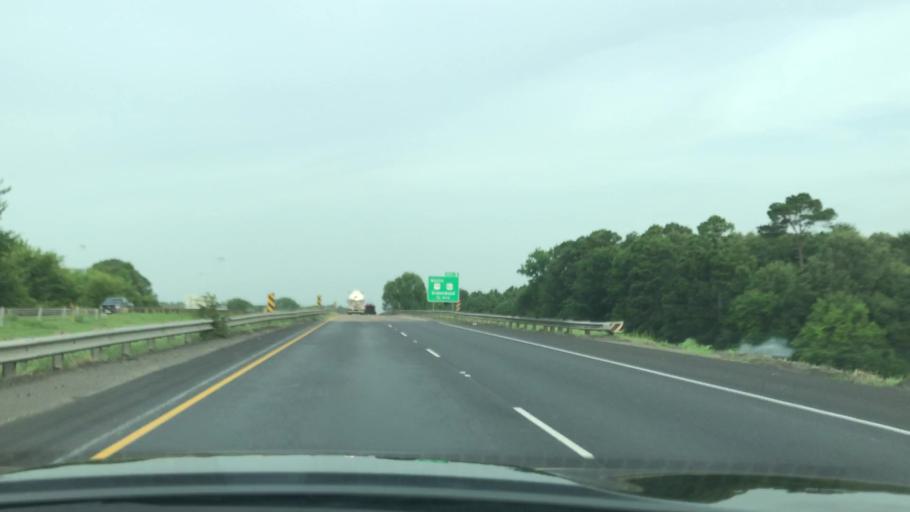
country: US
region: Louisiana
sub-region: Caddo Parish
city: Greenwood
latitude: 32.4439
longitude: -93.9365
